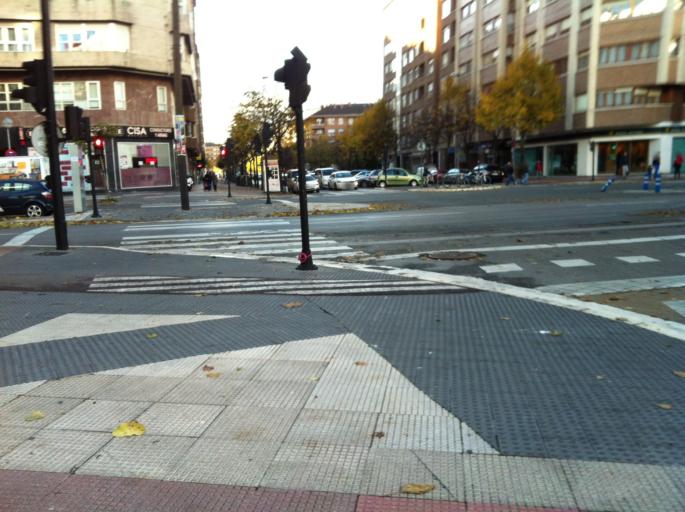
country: ES
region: Basque Country
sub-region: Provincia de Alava
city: Gasteiz / Vitoria
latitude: 42.8442
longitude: -2.6823
